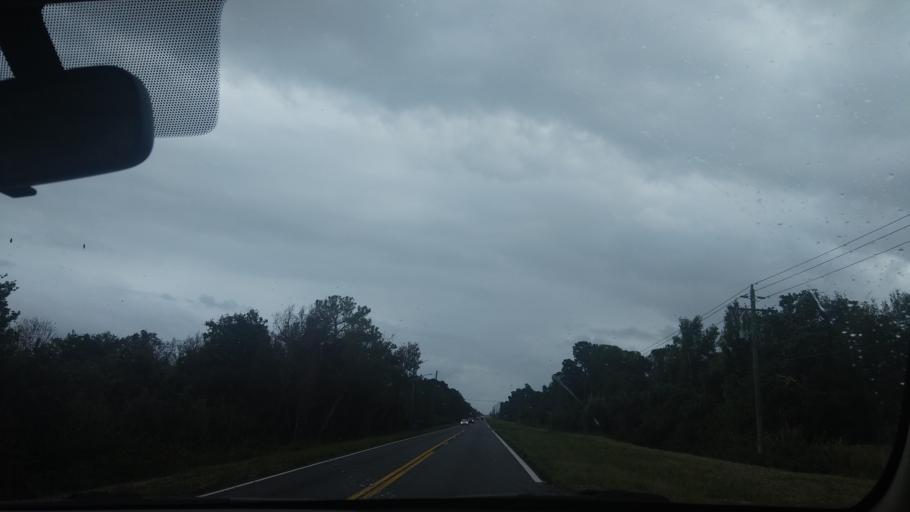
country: US
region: Florida
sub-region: Brevard County
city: Grant-Valkaria
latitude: 27.9458
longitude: -80.6227
